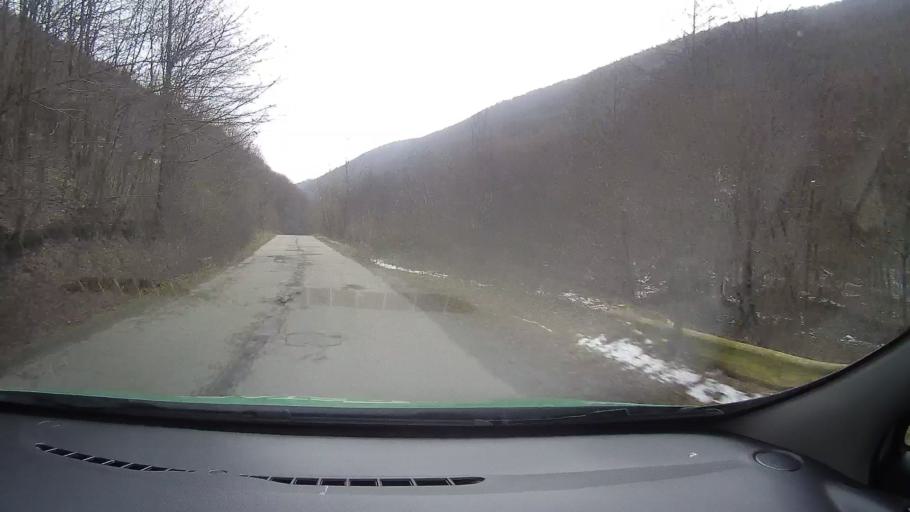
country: RO
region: Hunedoara
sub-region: Comuna Balsa
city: Balsa
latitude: 45.9991
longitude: 23.1503
